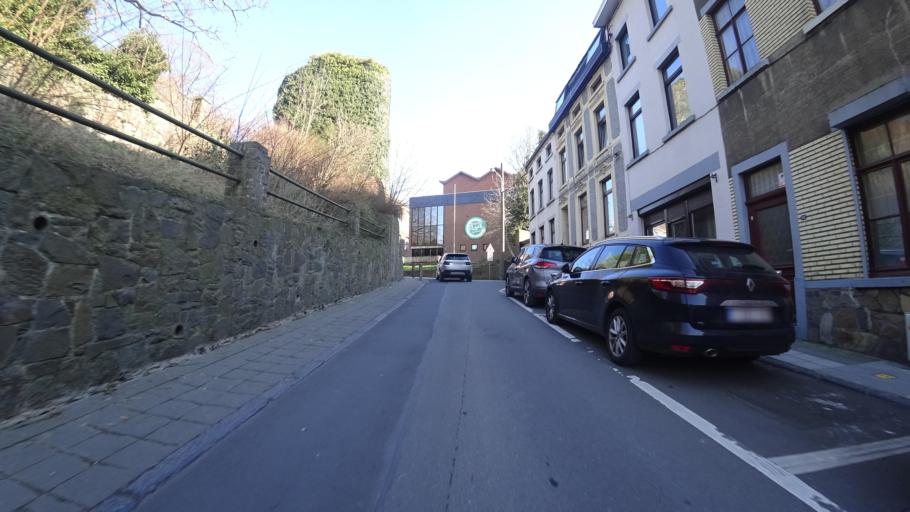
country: BE
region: Wallonia
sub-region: Province de Namur
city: Gembloux
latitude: 50.5593
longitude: 4.6934
